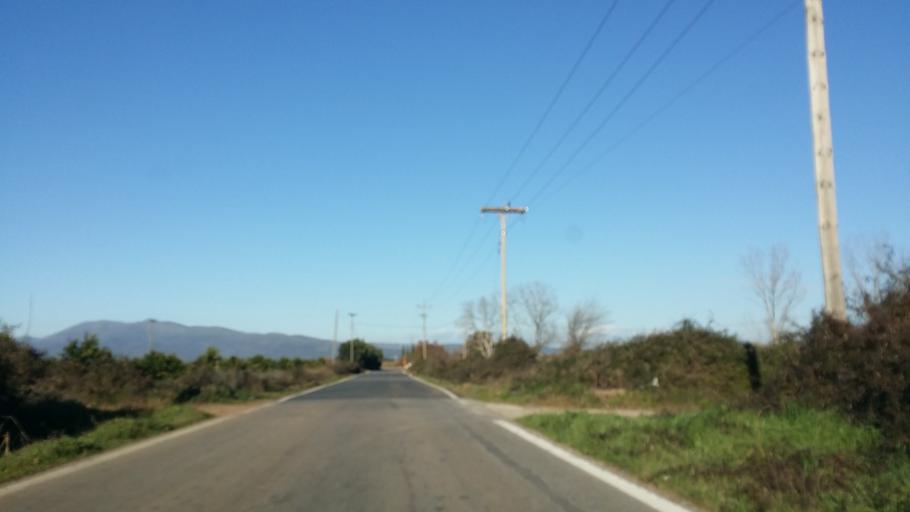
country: GR
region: West Greece
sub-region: Nomos Aitolias kai Akarnanias
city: Angelokastro
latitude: 38.6202
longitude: 21.2285
